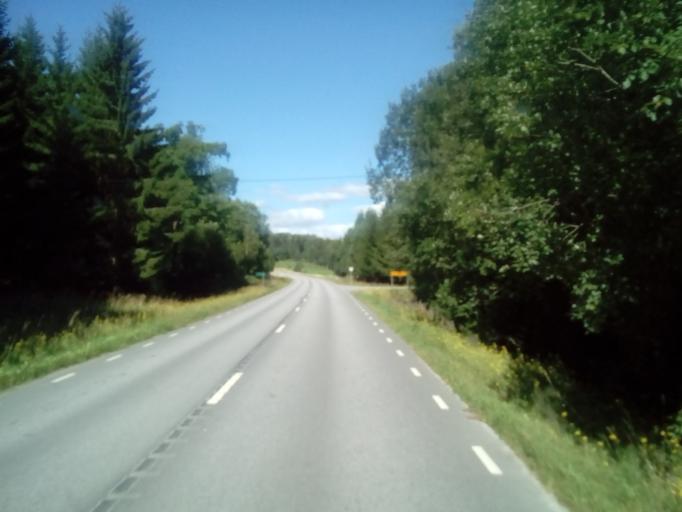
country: SE
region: Kalmar
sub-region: Vimmerby Kommun
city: Sodra Vi
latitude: 57.9181
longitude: 15.9486
